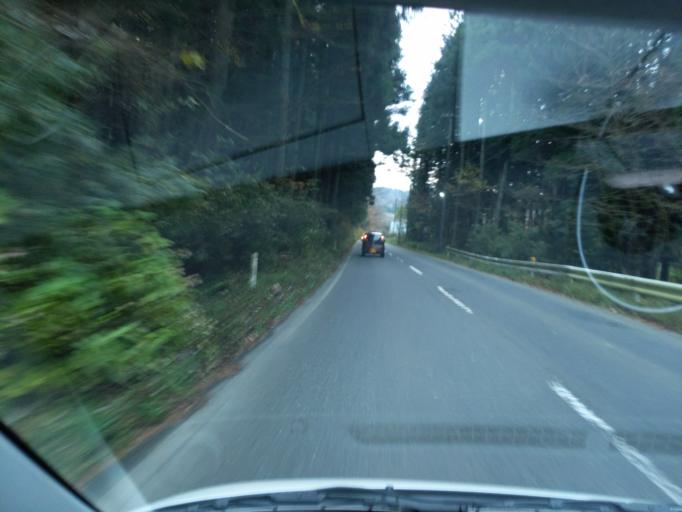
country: JP
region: Iwate
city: Mizusawa
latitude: 39.0254
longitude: 141.3327
